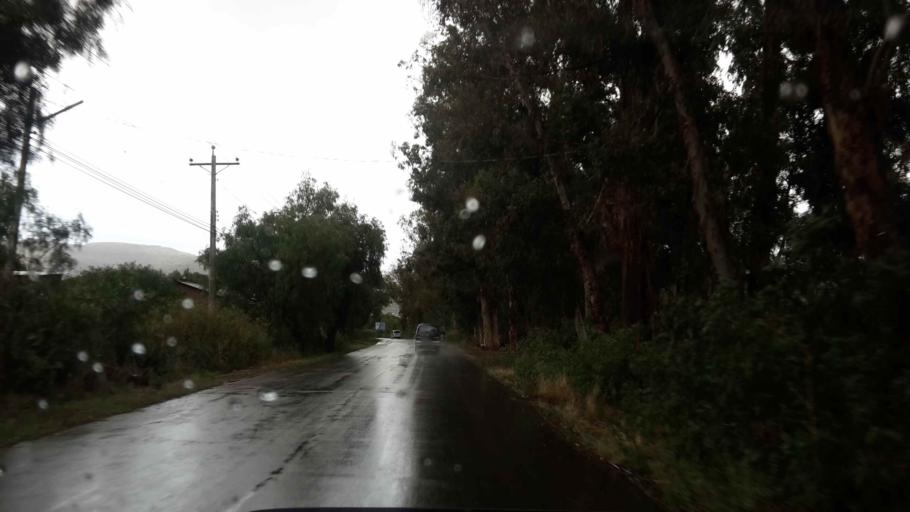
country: BO
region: Cochabamba
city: Tarata
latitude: -17.5423
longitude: -66.1064
